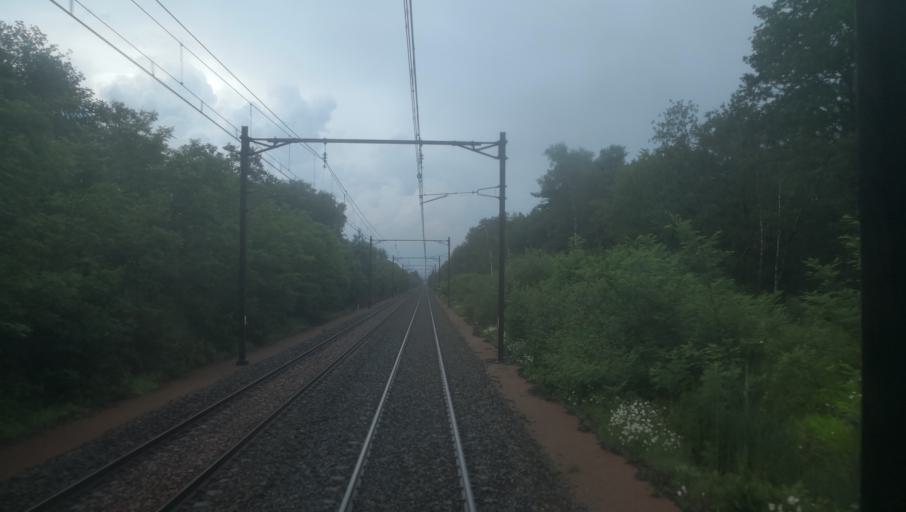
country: FR
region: Centre
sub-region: Departement du Loiret
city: Saint-Cyr-en-Val
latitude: 47.7824
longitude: 1.9405
